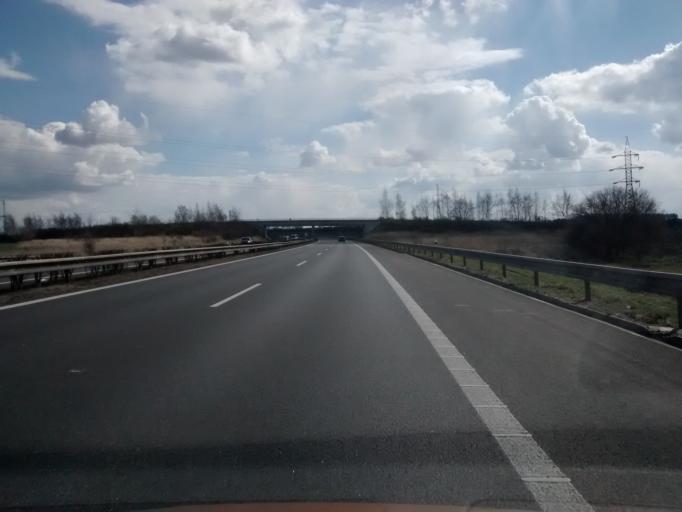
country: CZ
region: Central Bohemia
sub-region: Okres Melnik
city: Veltrusy
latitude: 50.2803
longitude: 14.3533
